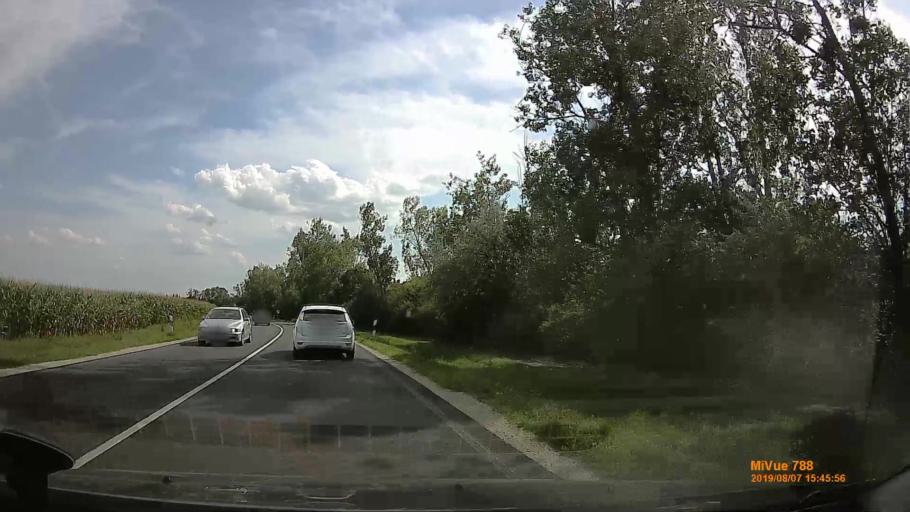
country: HU
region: Vas
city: Szombathely
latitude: 47.1910
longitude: 16.6201
